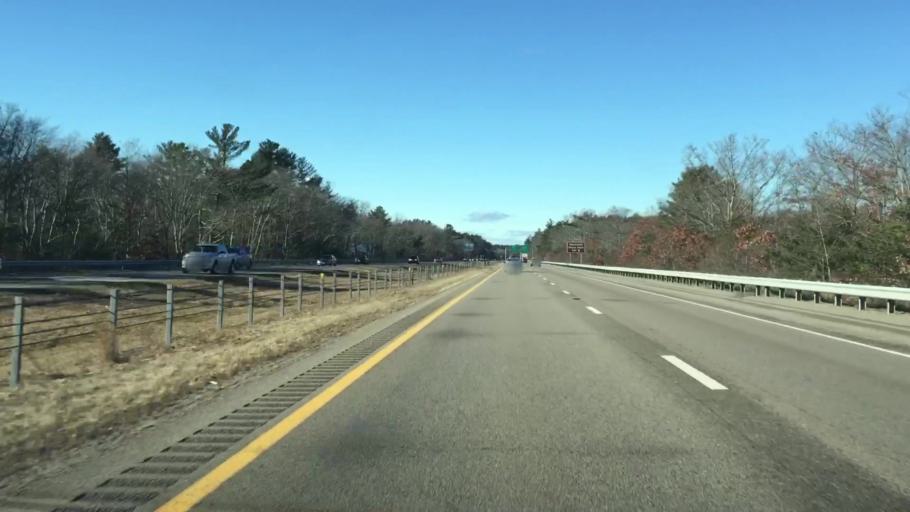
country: US
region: Massachusetts
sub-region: Plymouth County
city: Middleborough Center
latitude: 41.8905
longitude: -70.9404
